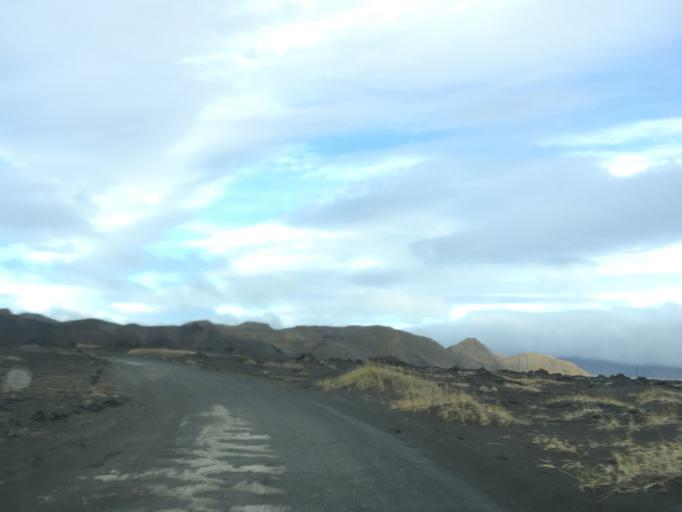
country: IS
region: South
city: Vestmannaeyjar
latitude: 64.0979
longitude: -19.1092
